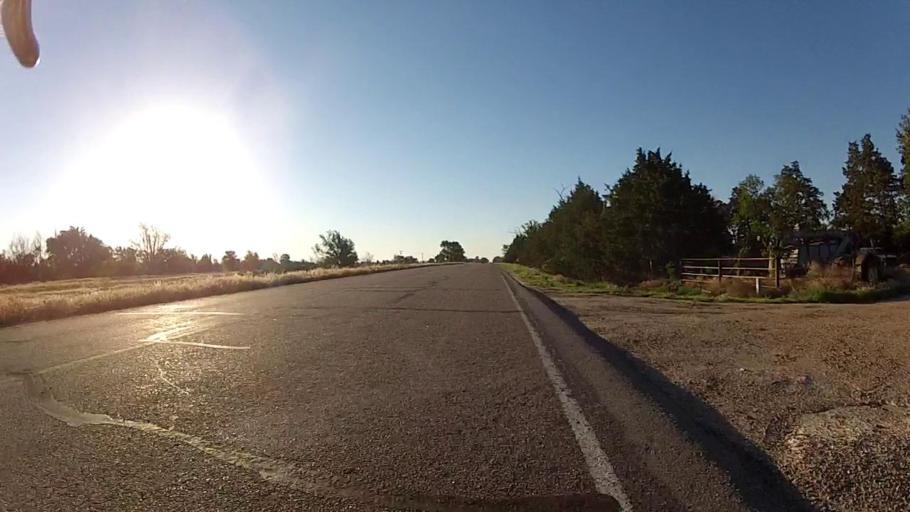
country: US
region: Kansas
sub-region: Ford County
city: Dodge City
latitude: 37.7168
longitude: -99.9382
